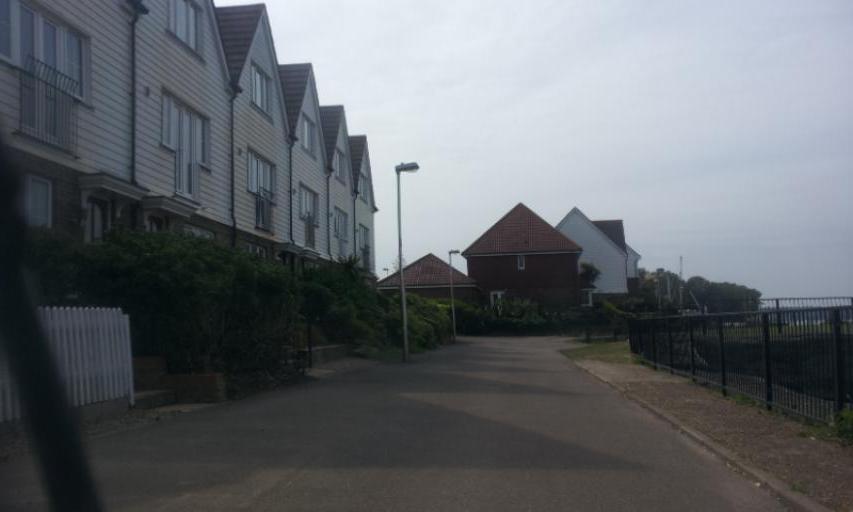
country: GB
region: England
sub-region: Kent
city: Gillingham
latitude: 51.3920
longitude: 0.5715
